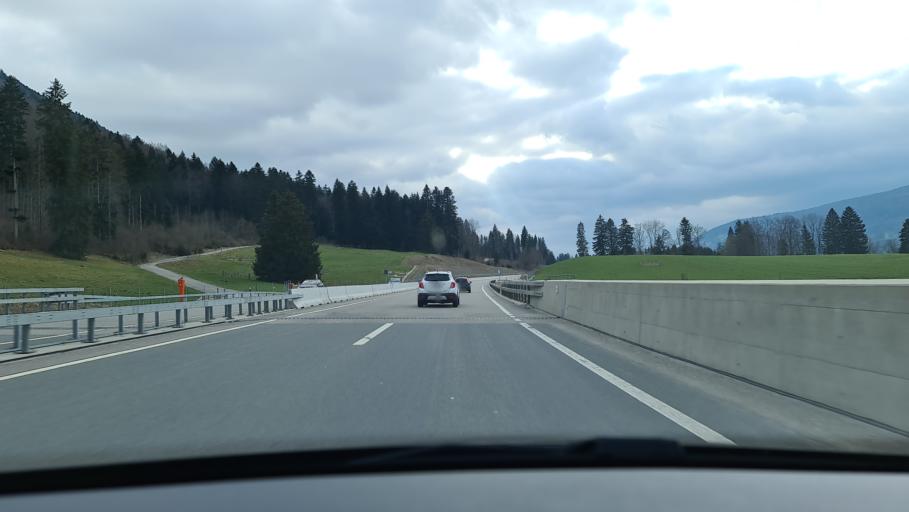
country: CH
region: Bern
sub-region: Jura bernois
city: Court
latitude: 47.2325
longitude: 7.3300
